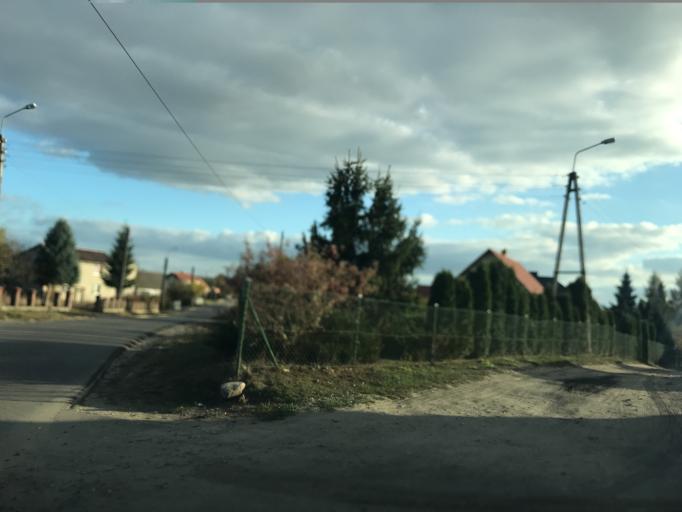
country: PL
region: Warmian-Masurian Voivodeship
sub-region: Powiat dzialdowski
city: Lidzbark
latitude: 53.3451
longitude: 19.8232
